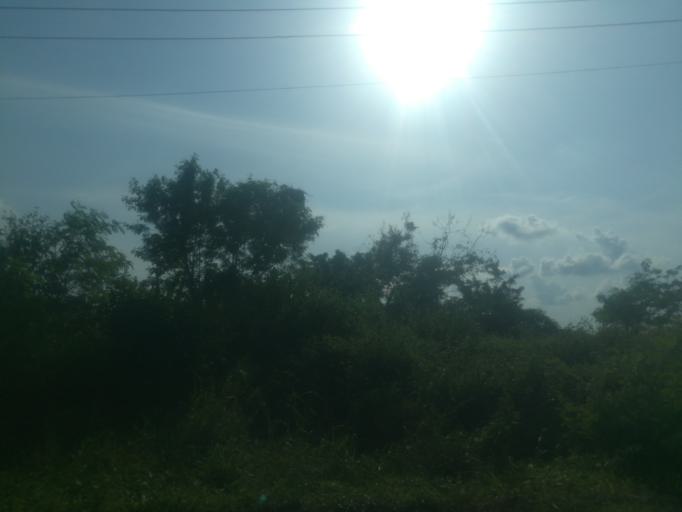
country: NG
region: Oyo
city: Ido
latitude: 7.3971
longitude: 3.7972
